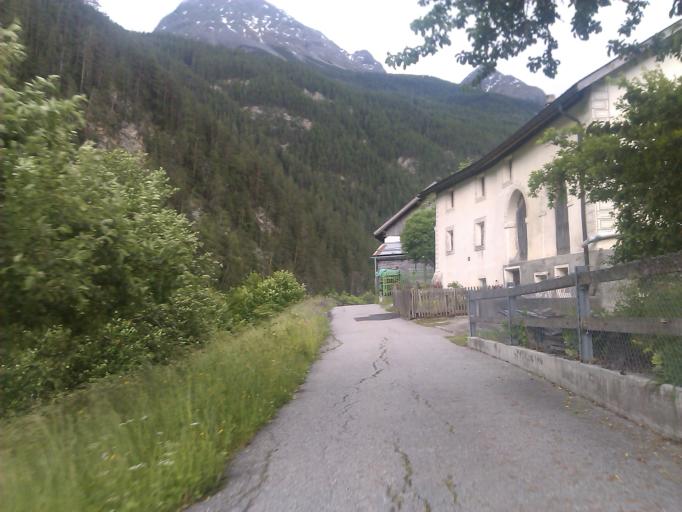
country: AT
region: Tyrol
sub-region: Politischer Bezirk Landeck
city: Nauders
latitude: 46.8808
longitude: 10.4590
